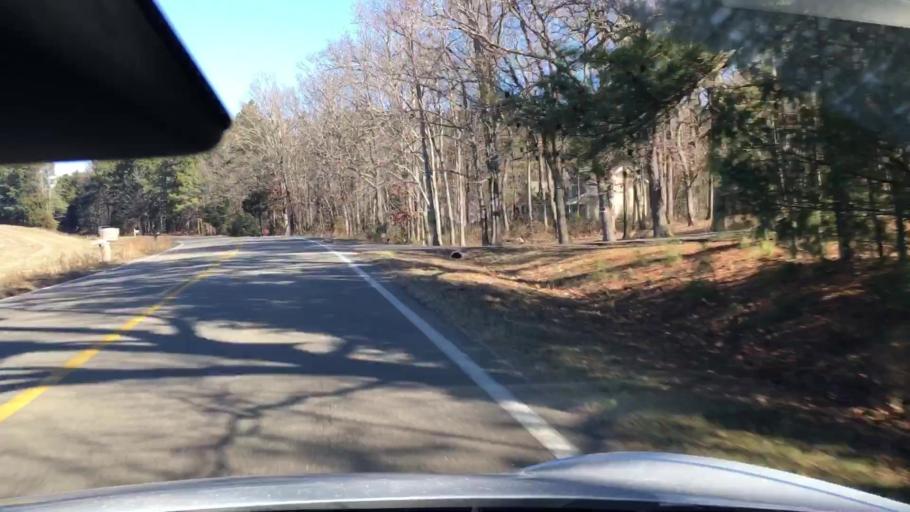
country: US
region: Virginia
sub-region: Powhatan County
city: Powhatan
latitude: 37.5346
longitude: -77.7990
